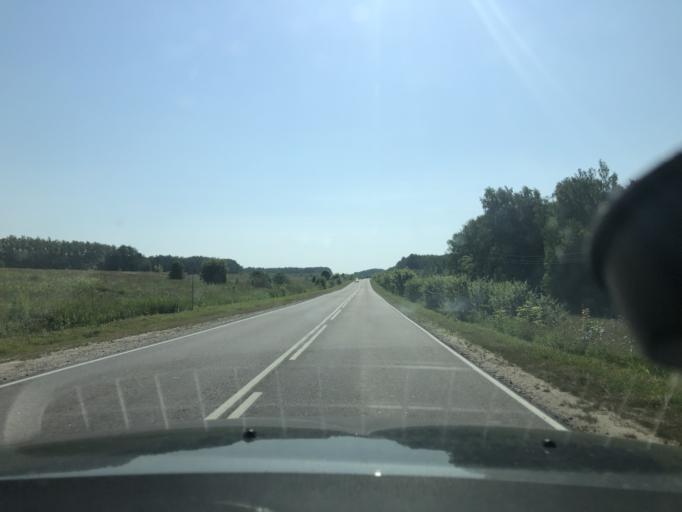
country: RU
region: Tula
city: Dubna
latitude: 54.1432
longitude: 36.9980
